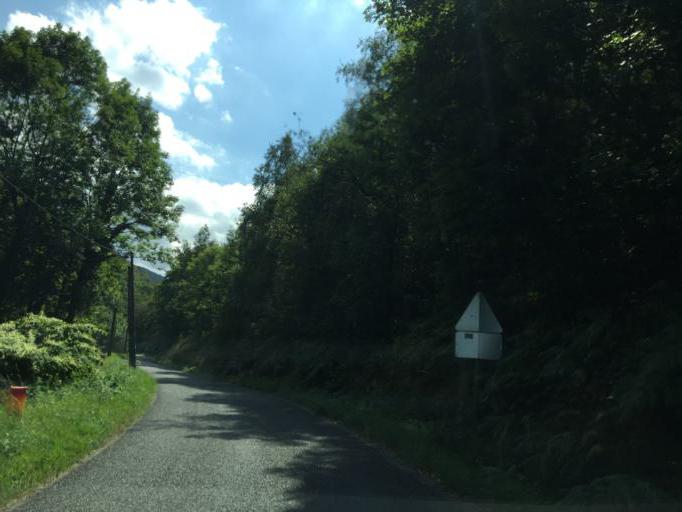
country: FR
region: Rhone-Alpes
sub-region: Departement de la Loire
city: Saint-Jean-Bonnefonds
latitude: 45.4240
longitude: 4.4378
